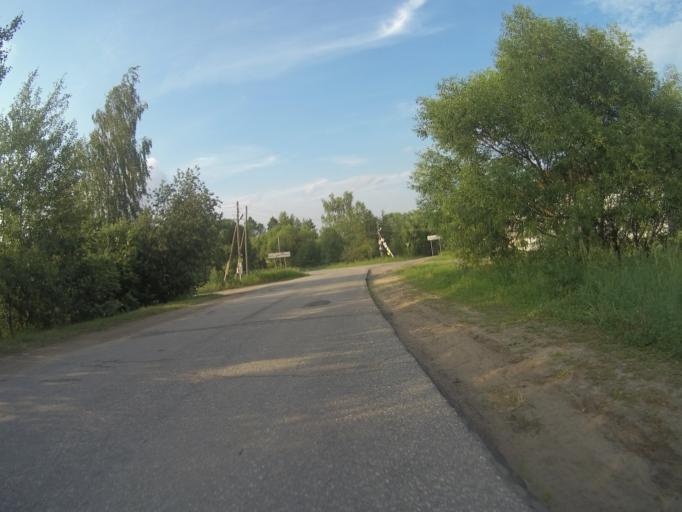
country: RU
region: Vladimir
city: Kommunar
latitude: 56.0744
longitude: 40.5391
